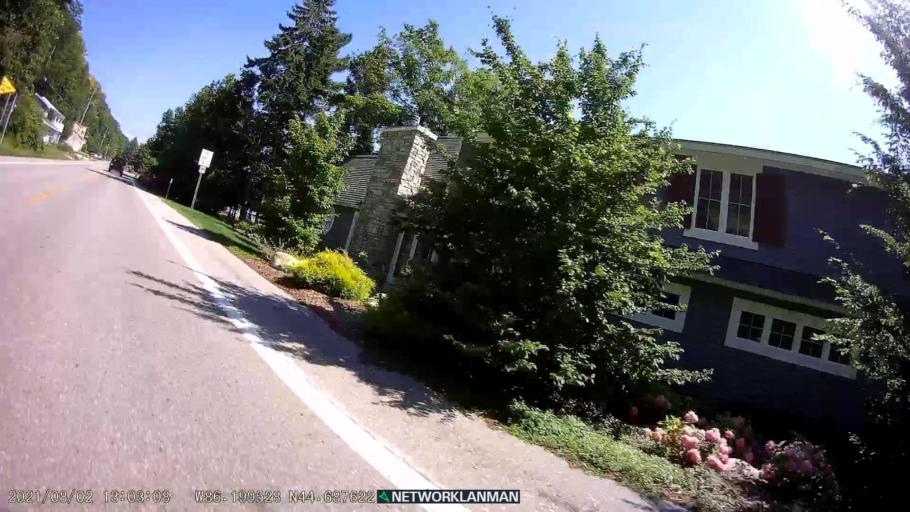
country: US
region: Michigan
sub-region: Benzie County
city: Frankfort
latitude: 44.6876
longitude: -86.1993
